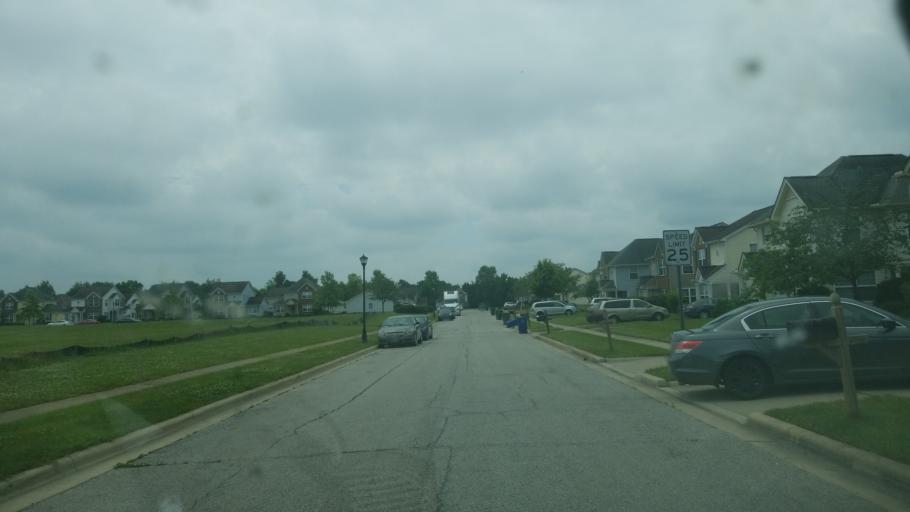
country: US
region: Ohio
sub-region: Franklin County
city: Reynoldsburg
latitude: 40.0015
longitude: -82.7958
